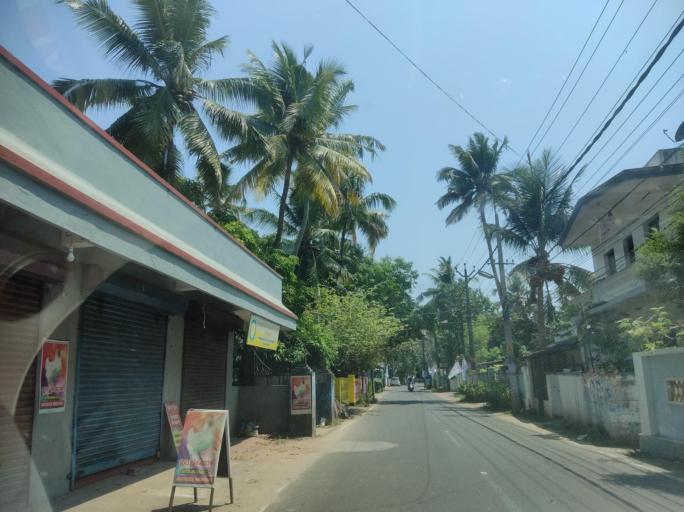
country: IN
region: Kerala
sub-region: Alappuzha
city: Arukutti
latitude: 9.8561
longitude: 76.2934
